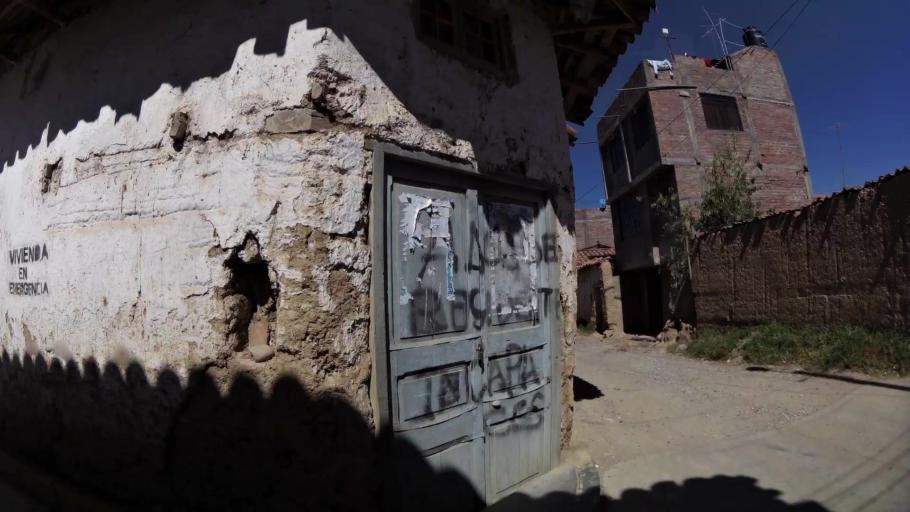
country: PE
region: Junin
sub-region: Provincia de Huancayo
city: San Jeronimo
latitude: -11.9469
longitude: -75.2856
